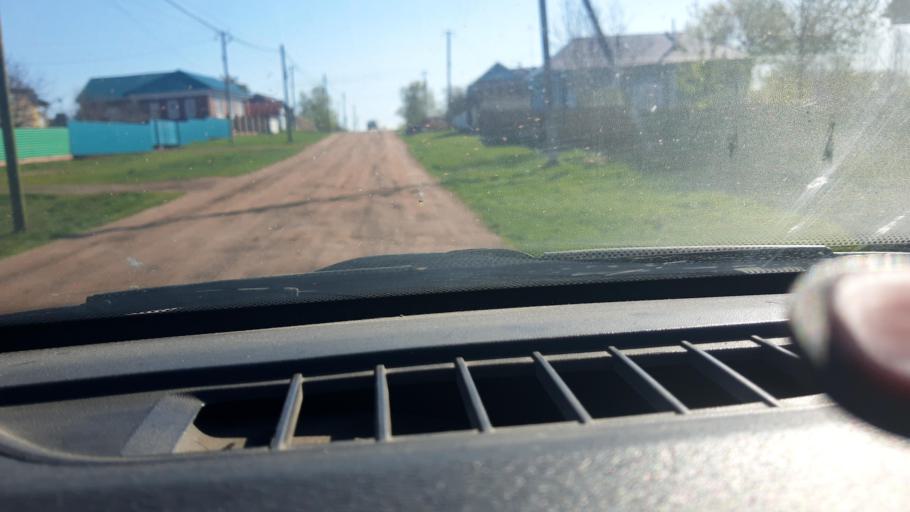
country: RU
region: Bashkortostan
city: Chishmy
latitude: 54.5942
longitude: 55.2685
